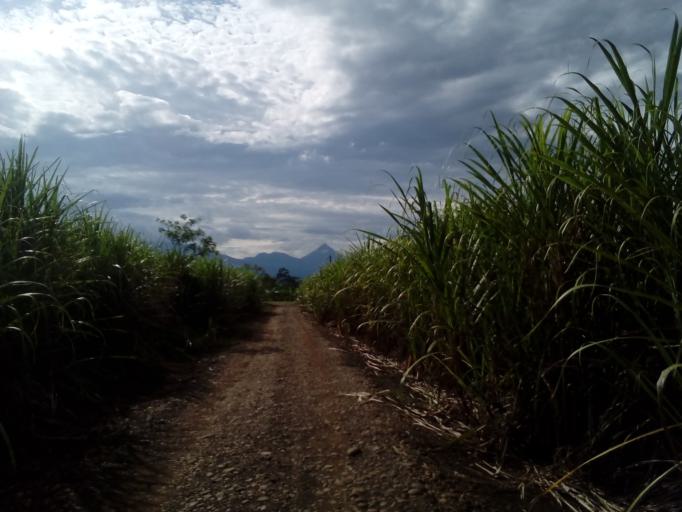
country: CR
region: Alajuela
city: Quesada
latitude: 10.4237
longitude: -84.4630
